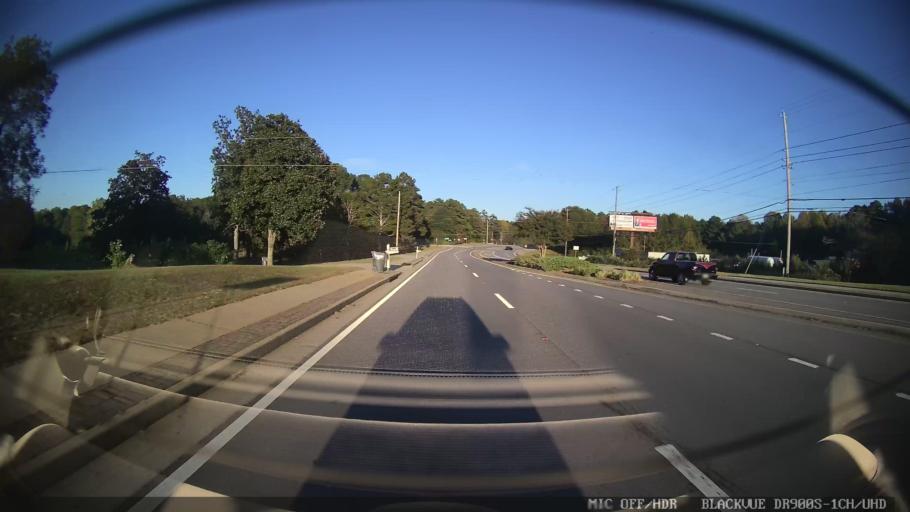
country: US
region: Georgia
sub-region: Clayton County
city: Jonesboro
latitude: 33.5405
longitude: -84.2985
